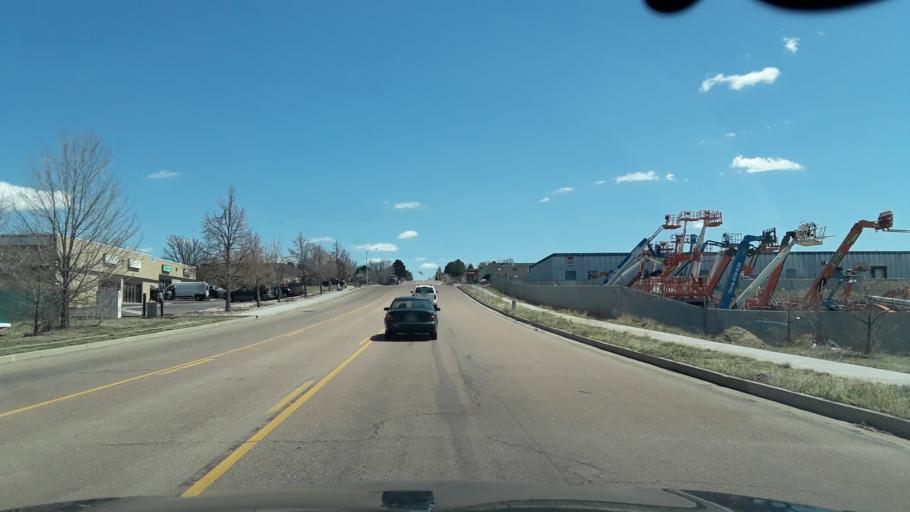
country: US
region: Colorado
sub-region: El Paso County
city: Cimarron Hills
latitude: 38.8462
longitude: -104.7136
